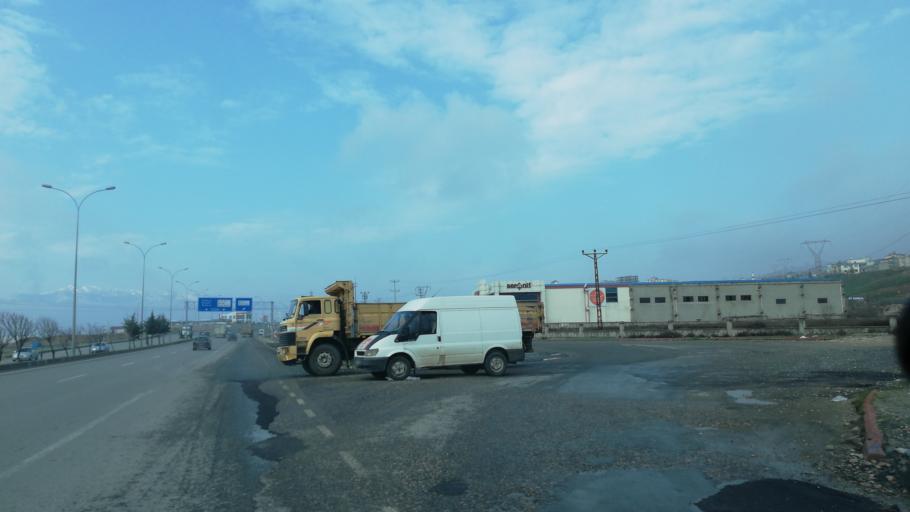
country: TR
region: Kahramanmaras
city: Kahramanmaras
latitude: 37.5641
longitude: 36.8958
